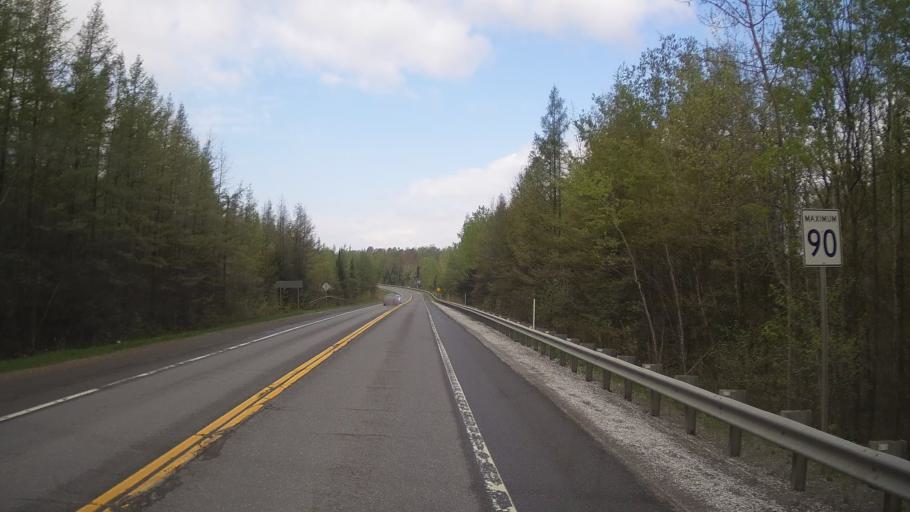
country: CA
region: Quebec
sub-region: Monteregie
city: Cowansville
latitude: 45.1984
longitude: -72.7227
